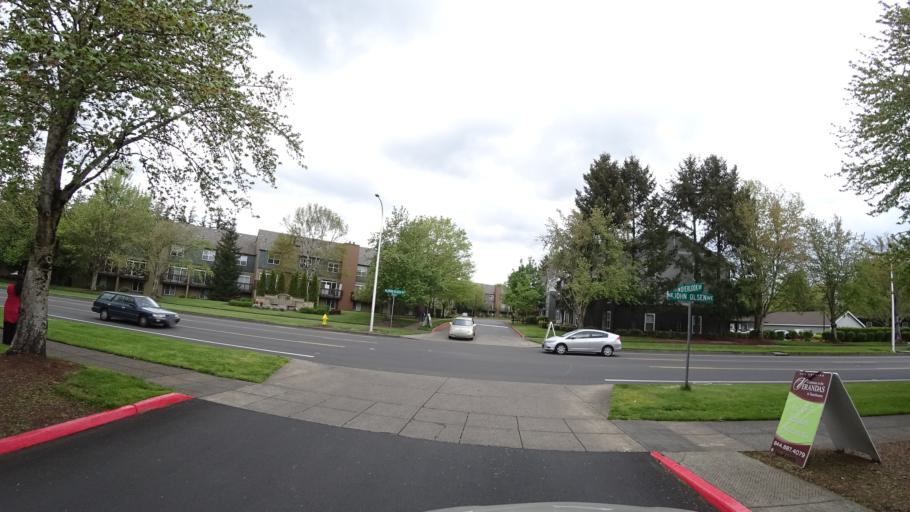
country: US
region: Oregon
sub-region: Washington County
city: Rockcreek
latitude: 45.5408
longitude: -122.8849
